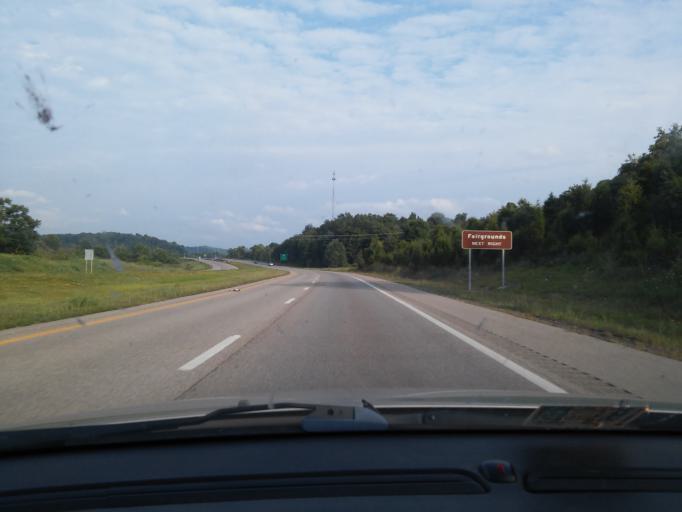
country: US
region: Ohio
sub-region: Gallia County
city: Gallipolis
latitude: 38.8532
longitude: -82.2451
